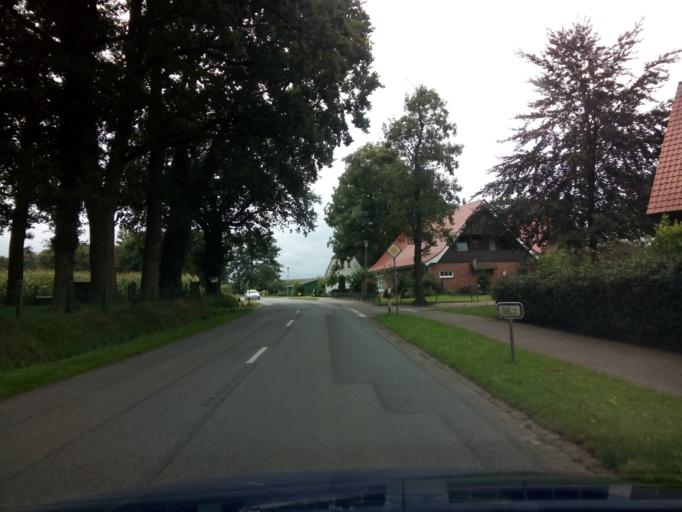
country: DE
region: Lower Saxony
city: Beverstedt
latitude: 53.4786
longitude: 8.8544
